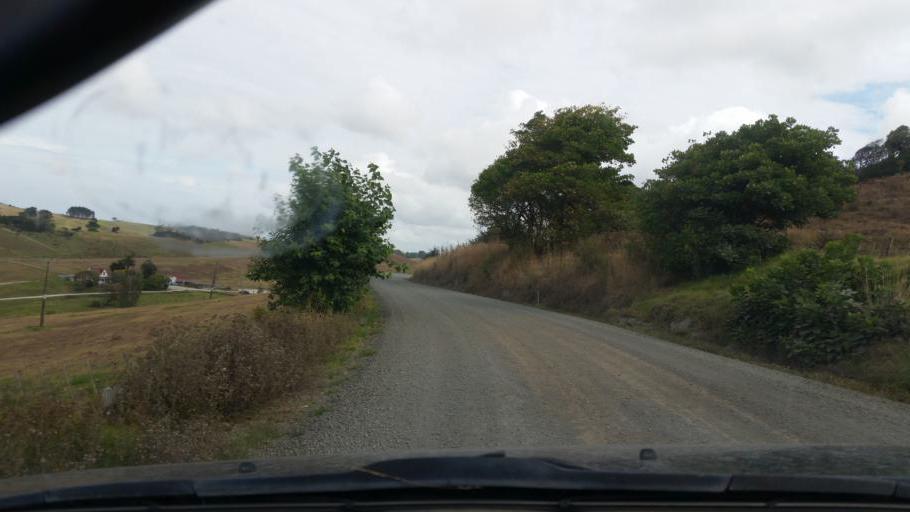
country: NZ
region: Northland
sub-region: Kaipara District
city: Dargaville
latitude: -35.9815
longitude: 173.9553
